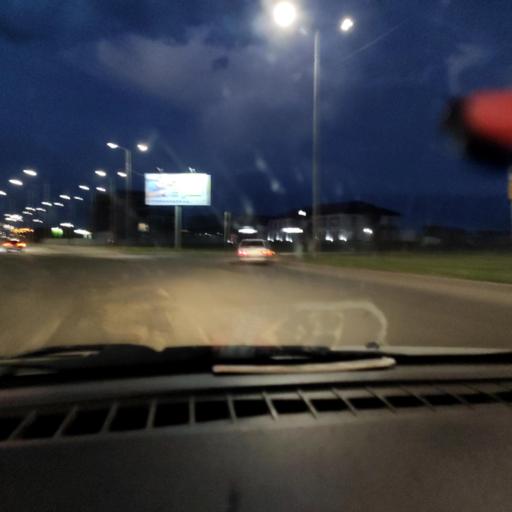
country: RU
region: Orenburg
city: Orenburg
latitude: 51.8046
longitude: 55.1648
